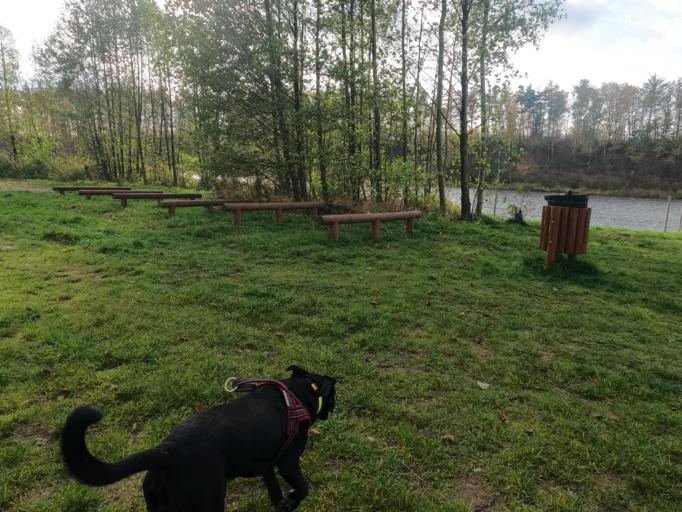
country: PL
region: Pomeranian Voivodeship
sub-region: Powiat starogardzki
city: Starogard Gdanski
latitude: 53.9719
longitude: 18.4801
